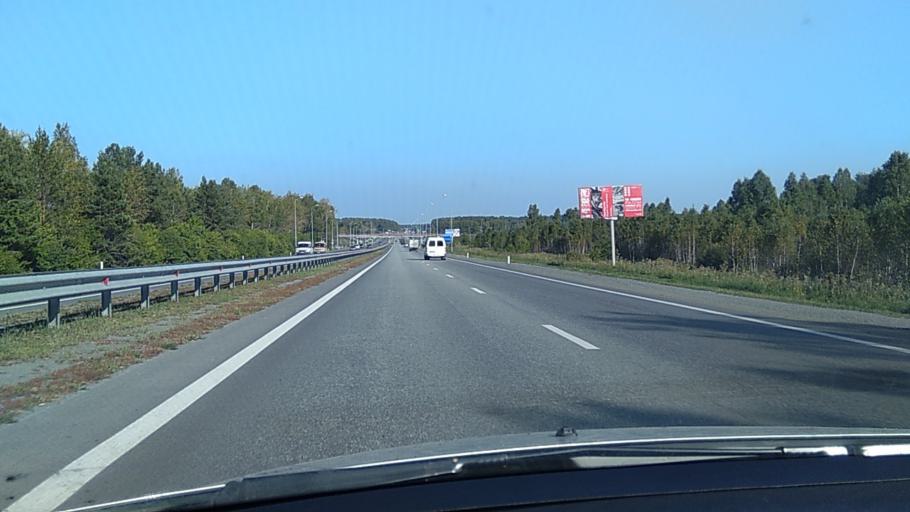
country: RU
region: Chelyabinsk
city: Sargazy
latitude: 55.0099
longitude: 61.2388
